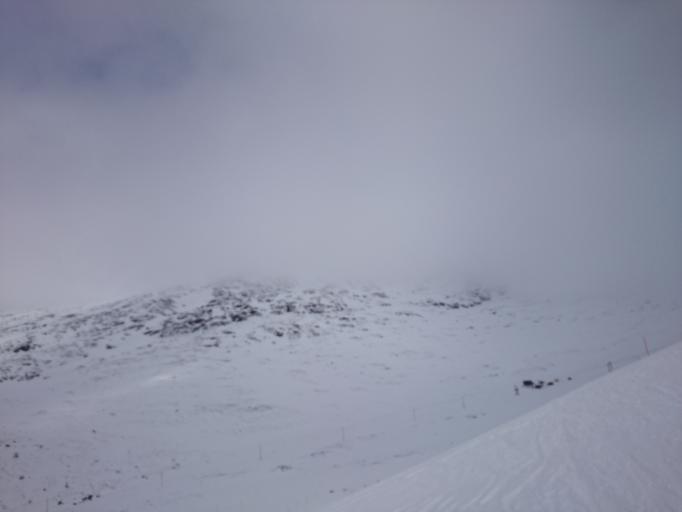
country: SE
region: Jaemtland
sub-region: Are Kommun
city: Are
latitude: 63.4331
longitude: 13.0543
